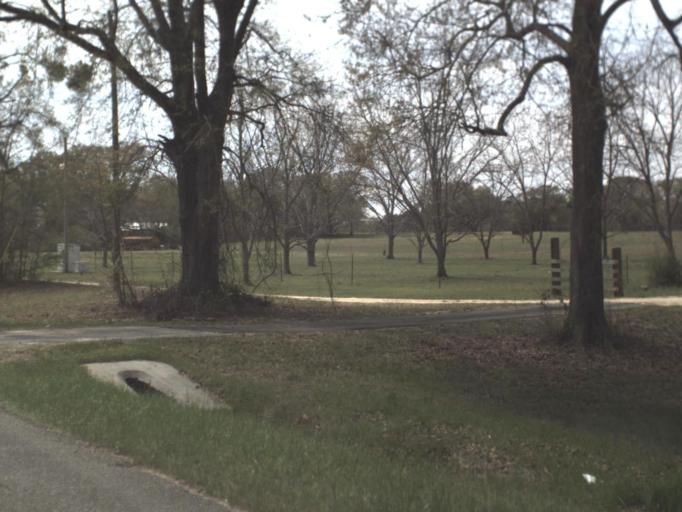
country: US
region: Florida
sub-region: Jackson County
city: Graceville
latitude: 30.8842
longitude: -85.5248
